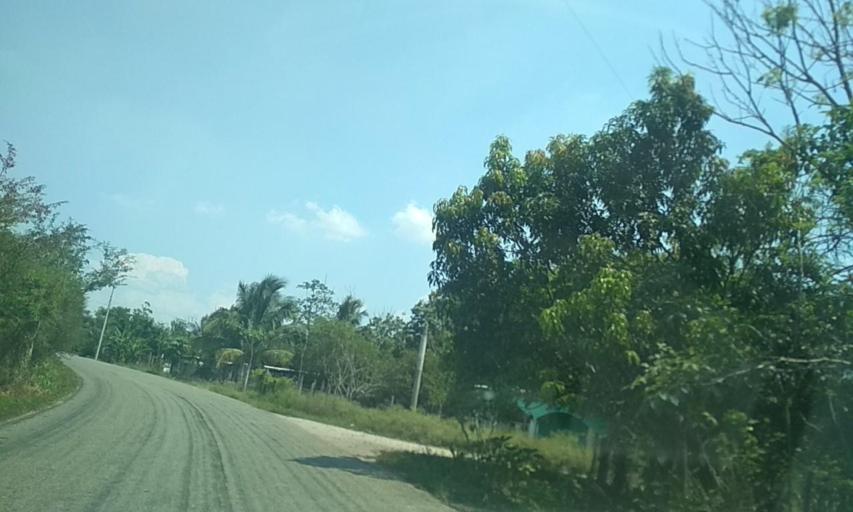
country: MX
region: Tabasco
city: Huimanguillo
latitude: 17.8051
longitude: -93.4931
